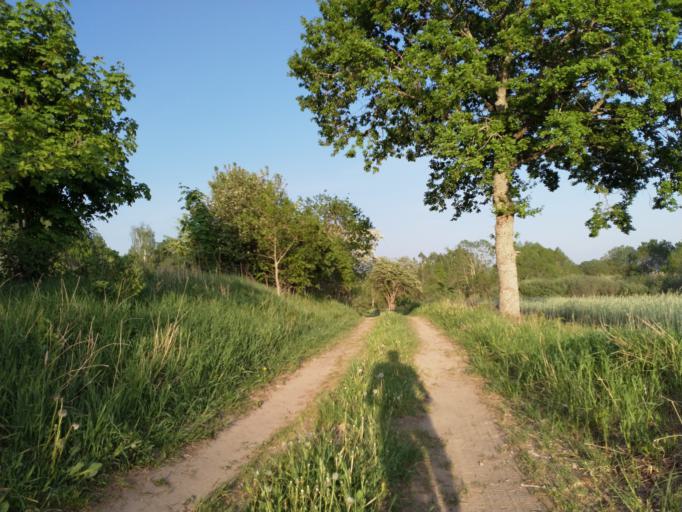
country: LV
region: Aizpute
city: Aizpute
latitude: 56.8323
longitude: 21.7808
